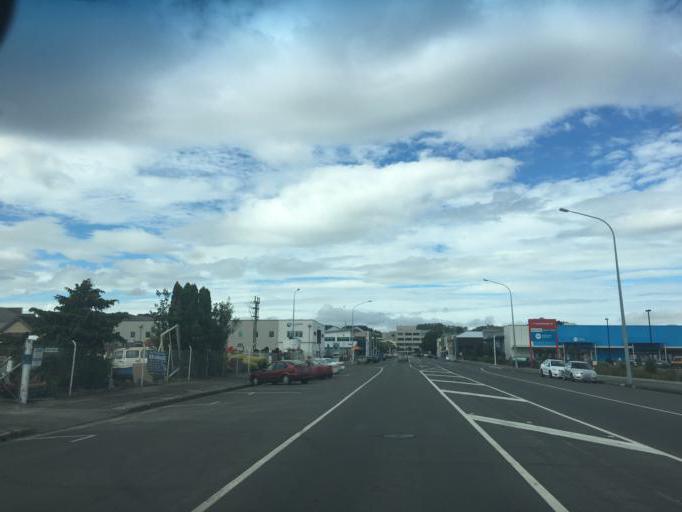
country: NZ
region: Gisborne
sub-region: Gisborne District
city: Gisborne
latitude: -38.6709
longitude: 178.0245
